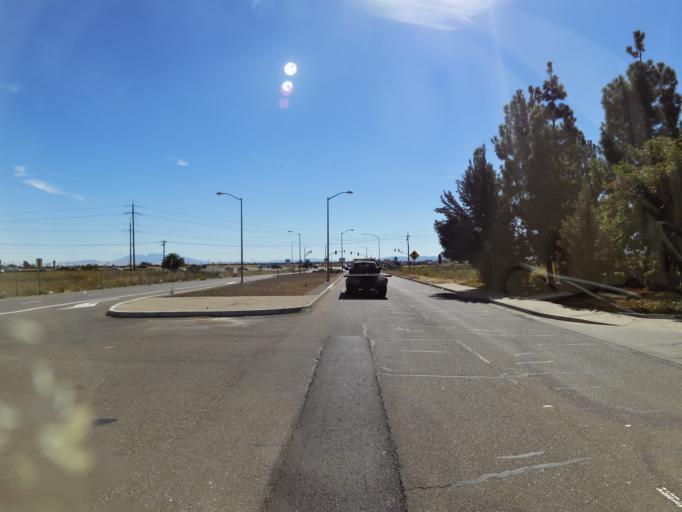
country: US
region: California
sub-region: Solano County
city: Suisun
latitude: 38.2432
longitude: -122.0502
